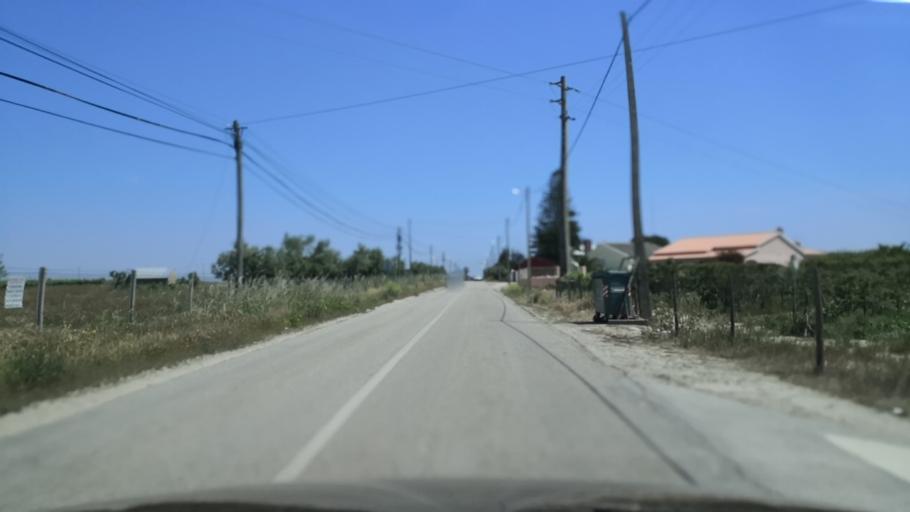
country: PT
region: Setubal
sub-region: Palmela
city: Palmela
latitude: 38.6019
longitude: -8.8061
